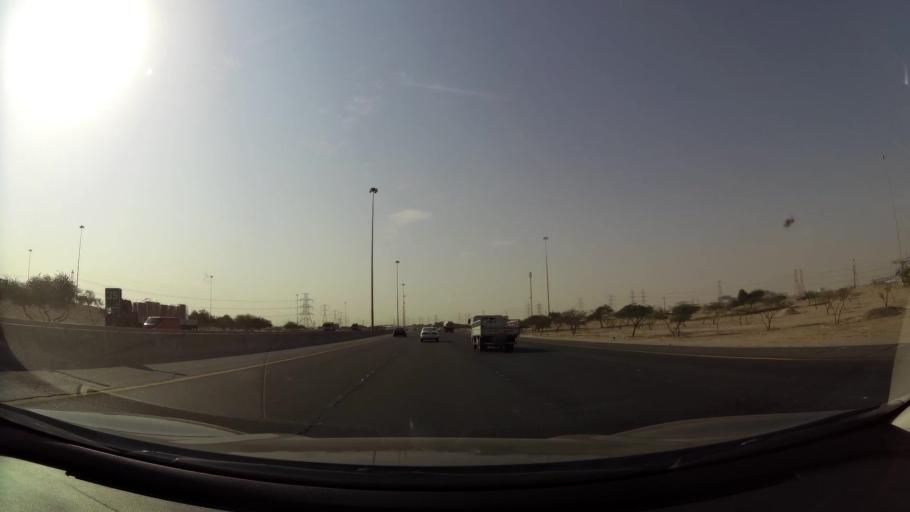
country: KW
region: Al Ahmadi
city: Al Ahmadi
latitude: 29.0298
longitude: 48.0918
